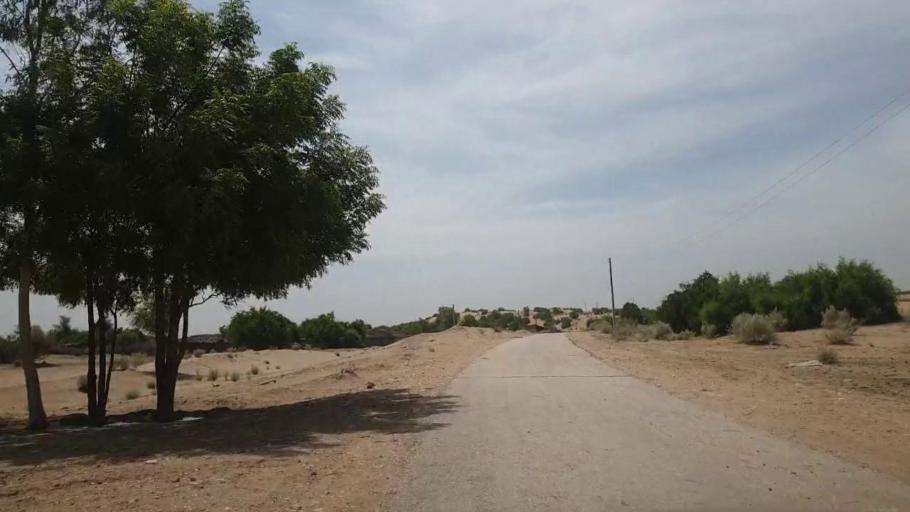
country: PK
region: Sindh
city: Kot Diji
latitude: 27.1087
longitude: 69.0768
